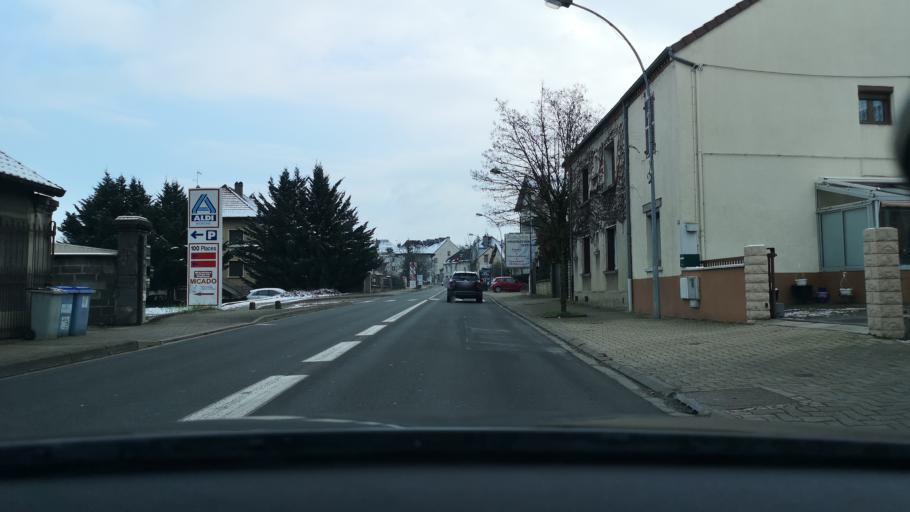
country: FR
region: Franche-Comte
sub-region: Departement du Jura
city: Montmorot
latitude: 46.6742
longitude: 5.5338
